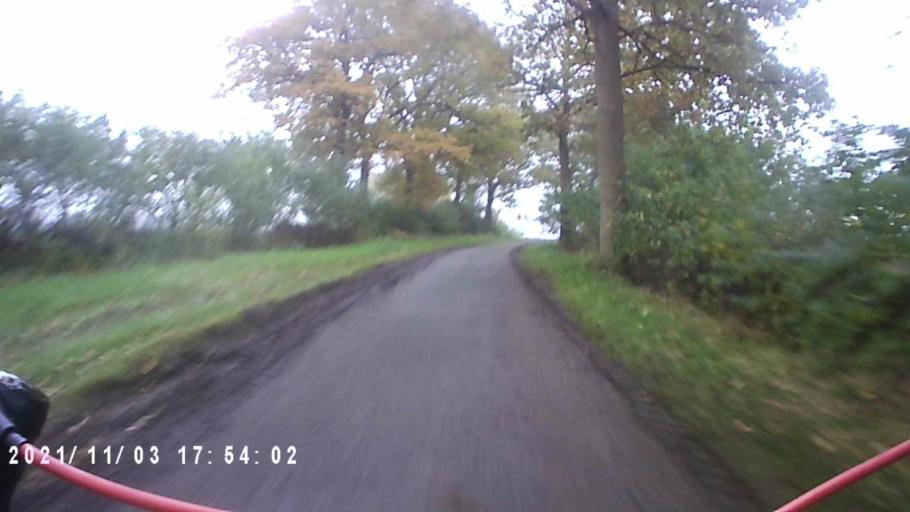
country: NL
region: Drenthe
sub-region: Gemeente Westerveld
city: Dwingeloo
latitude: 52.8397
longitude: 6.3248
